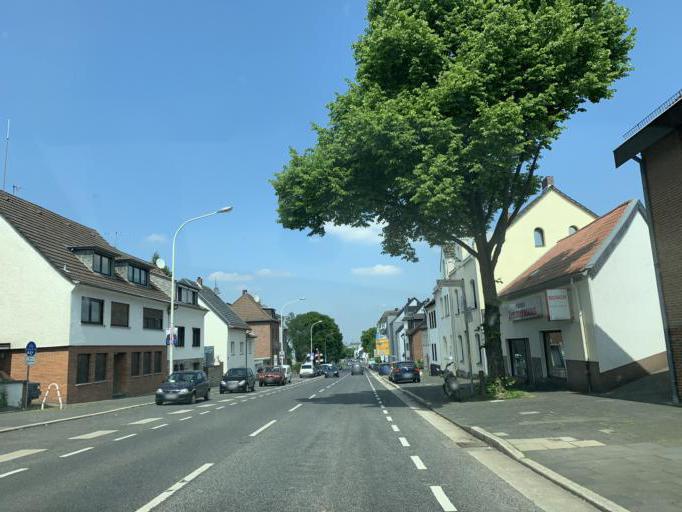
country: DE
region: North Rhine-Westphalia
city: Bruhl
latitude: 50.8167
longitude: 6.8908
